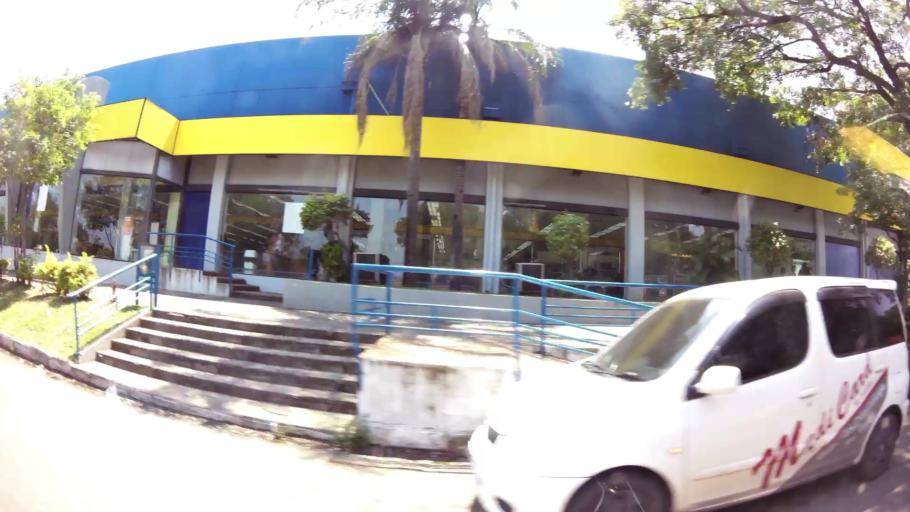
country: PY
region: Asuncion
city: Asuncion
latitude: -25.2993
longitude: -57.6404
